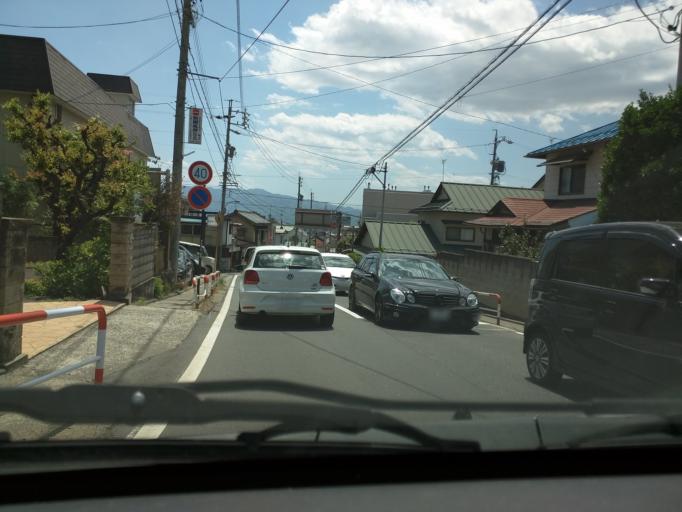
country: JP
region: Nagano
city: Nagano-shi
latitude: 36.6618
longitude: 138.1841
